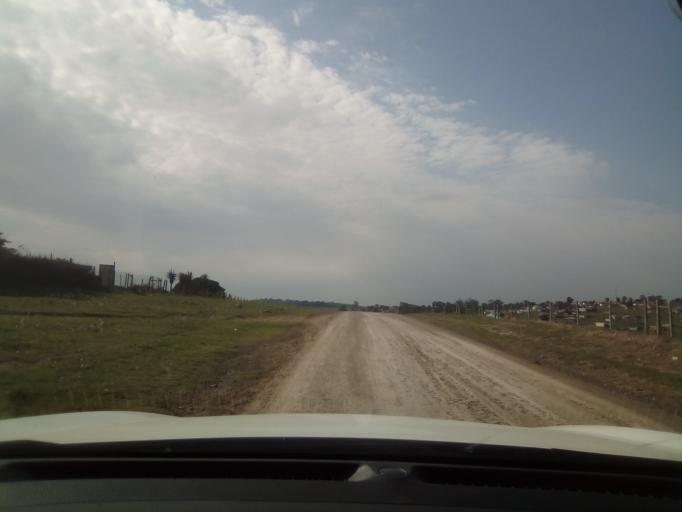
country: ZA
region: Eastern Cape
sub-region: Buffalo City Metropolitan Municipality
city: Bhisho
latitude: -32.9866
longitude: 27.2584
